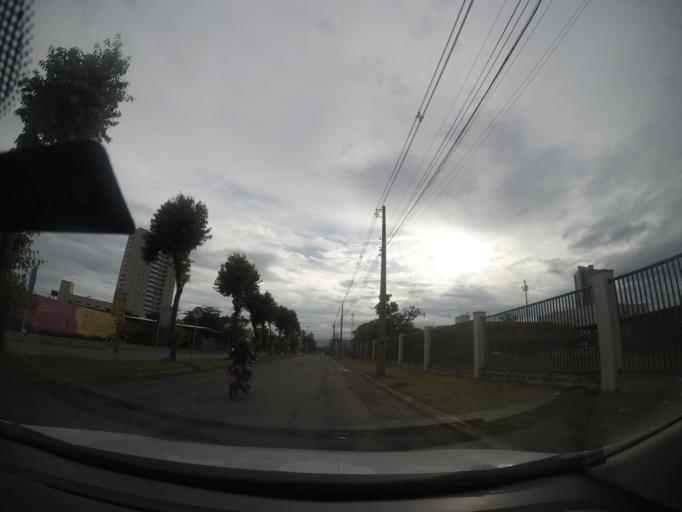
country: BR
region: Goias
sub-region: Goiania
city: Goiania
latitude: -16.7414
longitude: -49.2799
